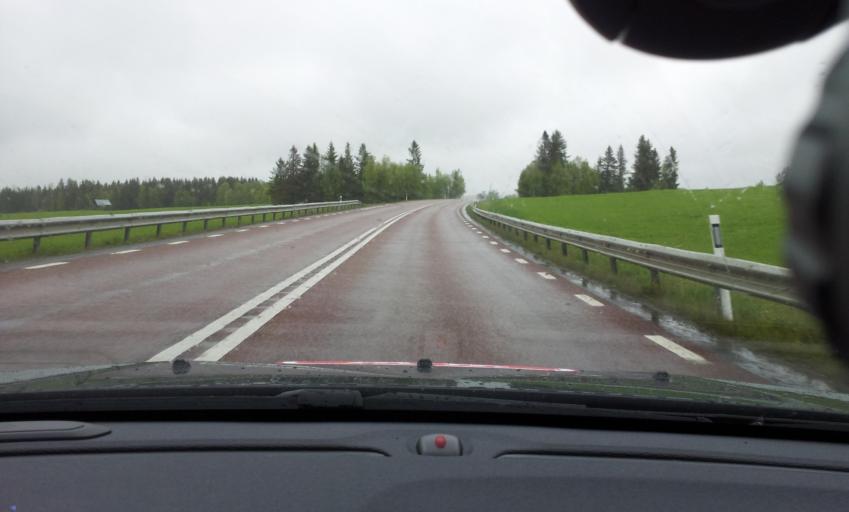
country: SE
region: Jaemtland
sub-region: Bergs Kommun
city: Hoverberg
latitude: 62.9806
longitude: 14.5682
